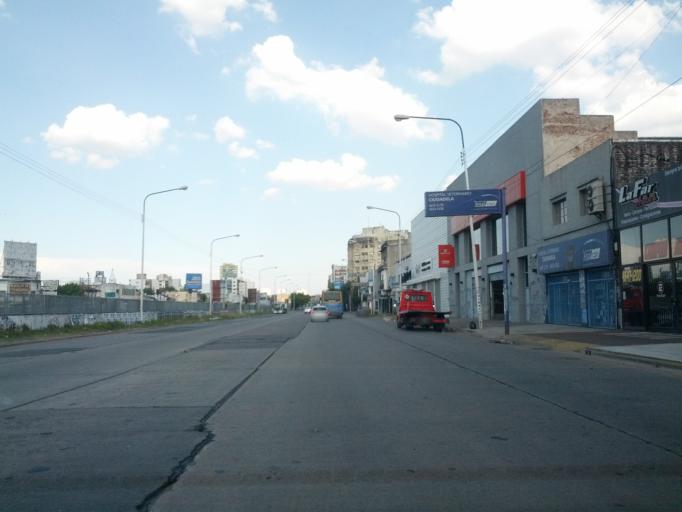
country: AR
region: Buenos Aires
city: San Justo
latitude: -34.6401
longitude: -58.5480
